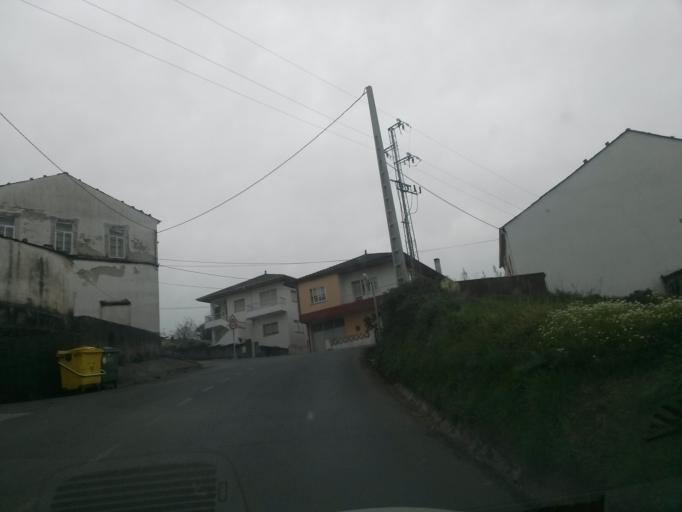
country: ES
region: Galicia
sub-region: Provincia de Lugo
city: Lugo
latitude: 43.0174
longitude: -7.5455
